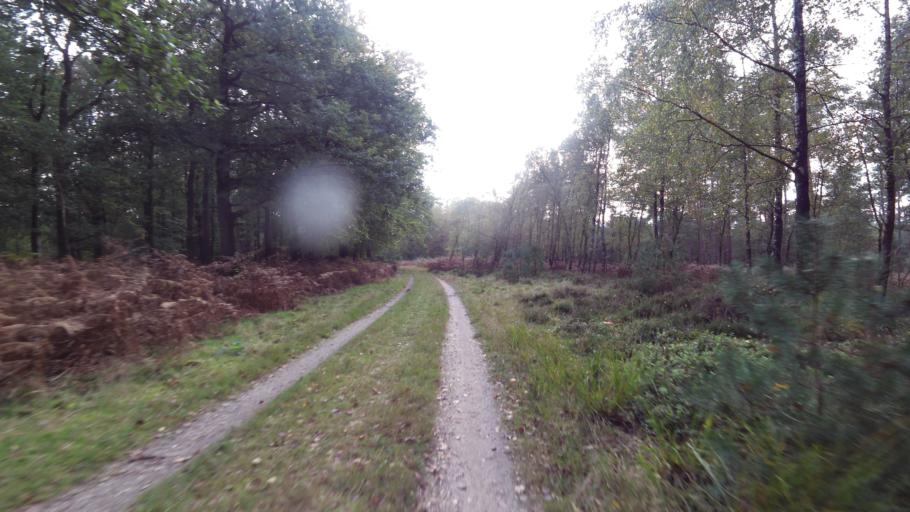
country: NL
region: Gelderland
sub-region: Gemeente Epe
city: Vaassen
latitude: 52.3228
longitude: 5.8723
